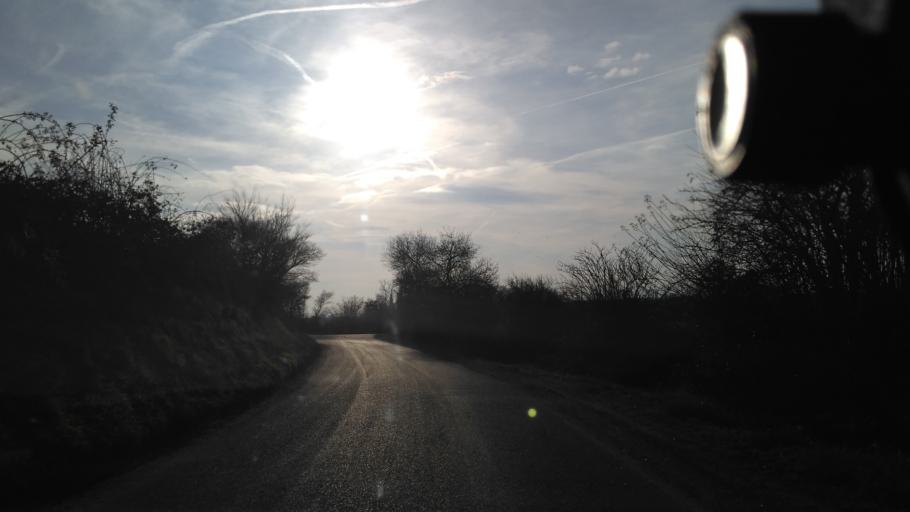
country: FR
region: Rhone-Alpes
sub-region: Departement de la Drome
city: Alixan
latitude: 44.9786
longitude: 5.0119
